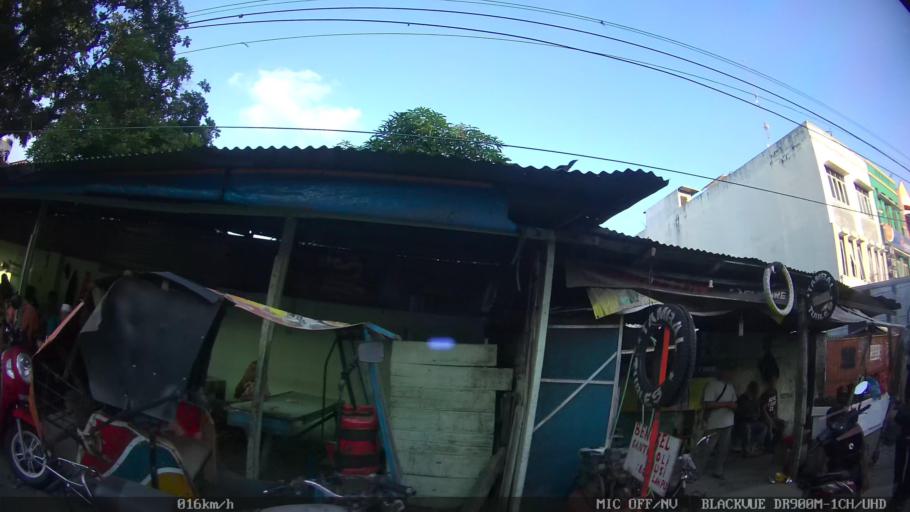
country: ID
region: North Sumatra
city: Medan
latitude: 3.6104
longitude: 98.6657
